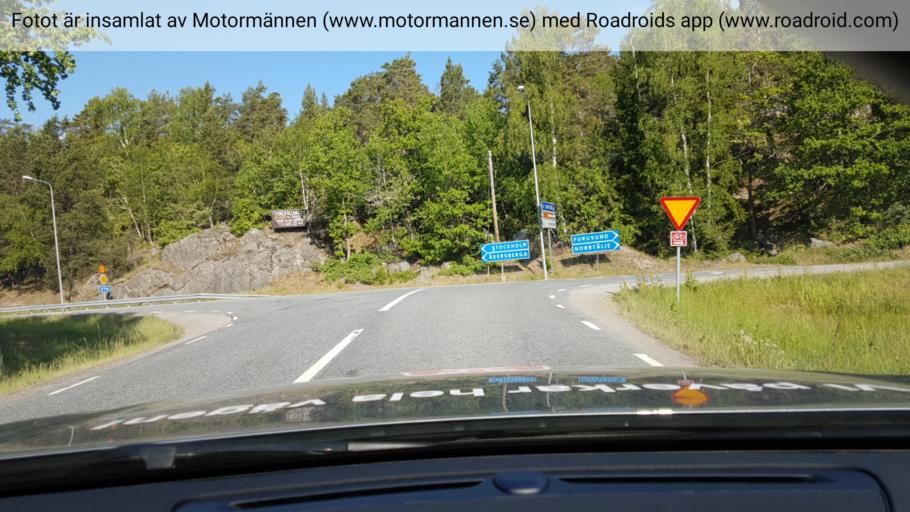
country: SE
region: Stockholm
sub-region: Varmdo Kommun
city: Hemmesta
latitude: 59.5568
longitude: 18.5572
